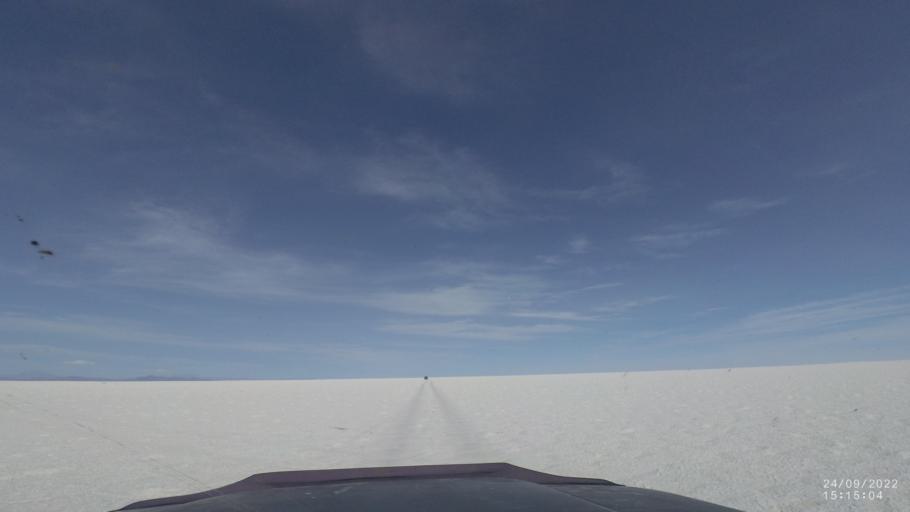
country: BO
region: Potosi
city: Colchani
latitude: -19.9697
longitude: -67.4491
